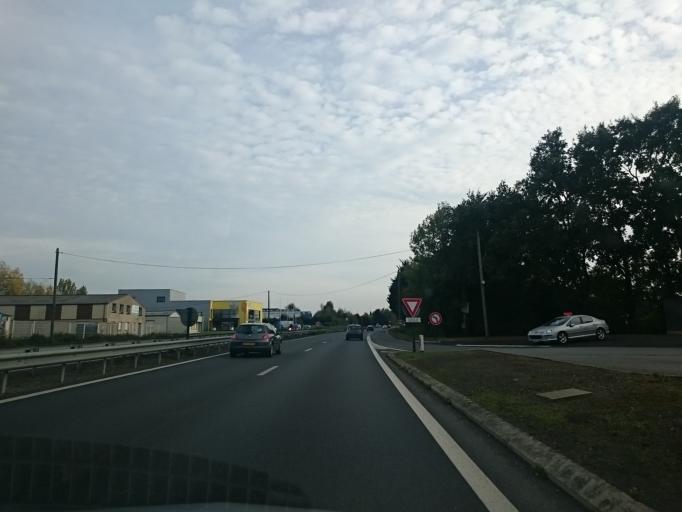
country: FR
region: Brittany
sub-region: Departement d'Ille-et-Vilaine
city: Vern-sur-Seiche
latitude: 48.0526
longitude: -1.6097
